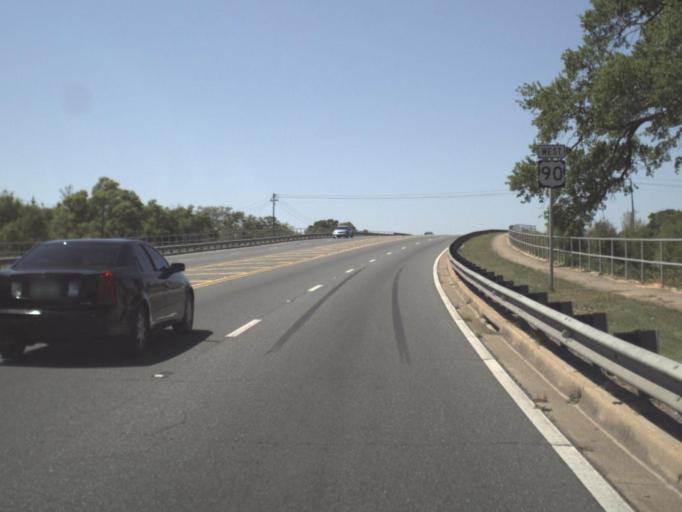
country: US
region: Florida
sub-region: Escambia County
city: West Pensacola
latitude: 30.4252
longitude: -87.2651
